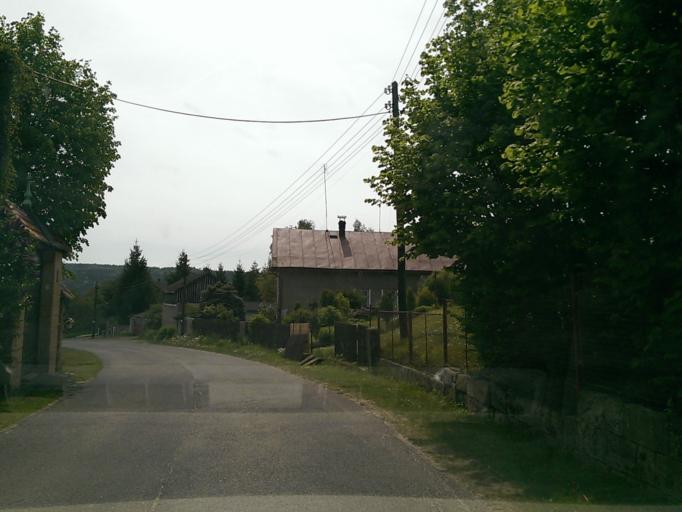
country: CZ
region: Central Bohemia
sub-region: Okres Mlada Boleslav
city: Zd'ar
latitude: 50.5439
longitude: 15.1212
